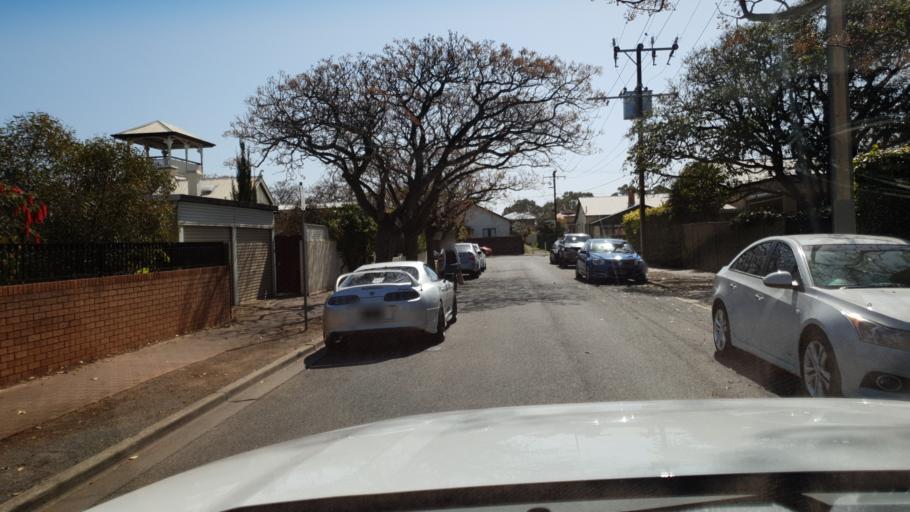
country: AU
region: South Australia
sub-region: Adelaide
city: Brighton
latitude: -35.0225
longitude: 138.5216
